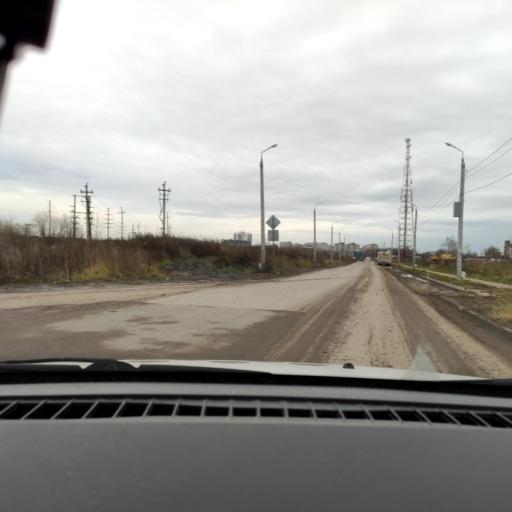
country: RU
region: Perm
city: Kondratovo
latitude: 57.9865
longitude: 56.1226
